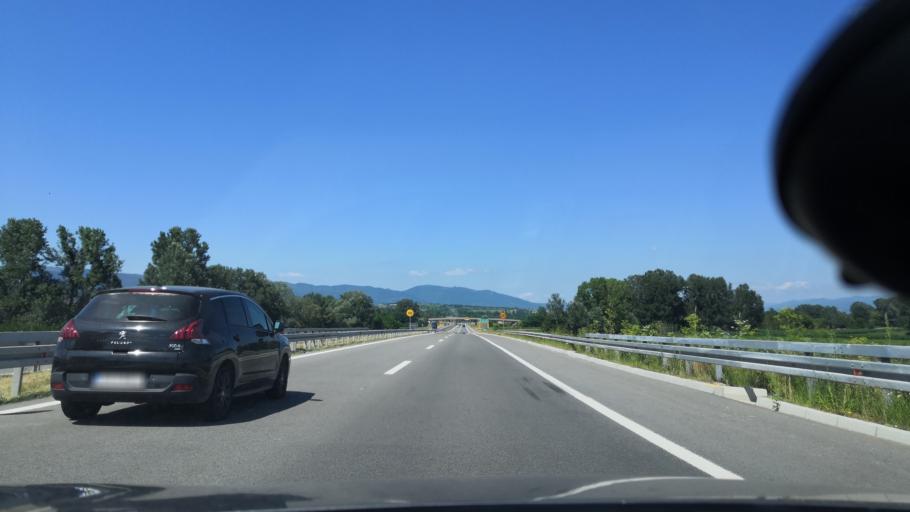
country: RS
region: Central Serbia
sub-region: Pcinjski Okrug
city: Bujanovac
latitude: 42.4609
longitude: 21.8080
